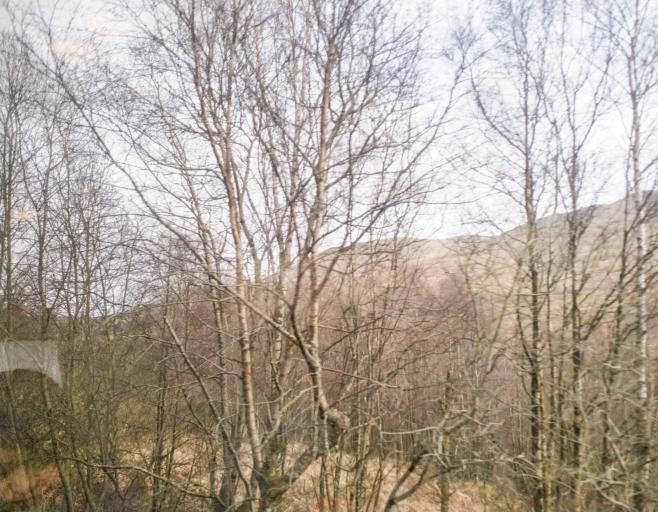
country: GB
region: Scotland
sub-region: Argyll and Bute
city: Garelochhead
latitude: 56.3543
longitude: -4.6872
